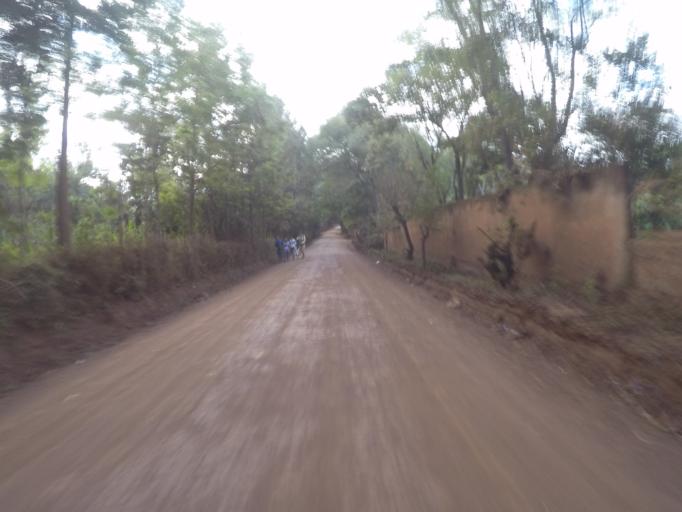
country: TZ
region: Arusha
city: Kiratu
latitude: -3.3362
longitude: 35.6668
